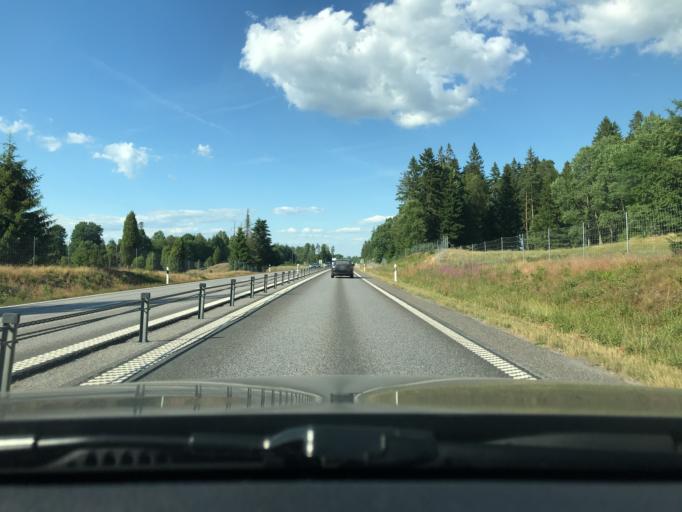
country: SE
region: Kronoberg
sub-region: Almhults Kommun
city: AElmhult
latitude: 56.5084
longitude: 14.1281
